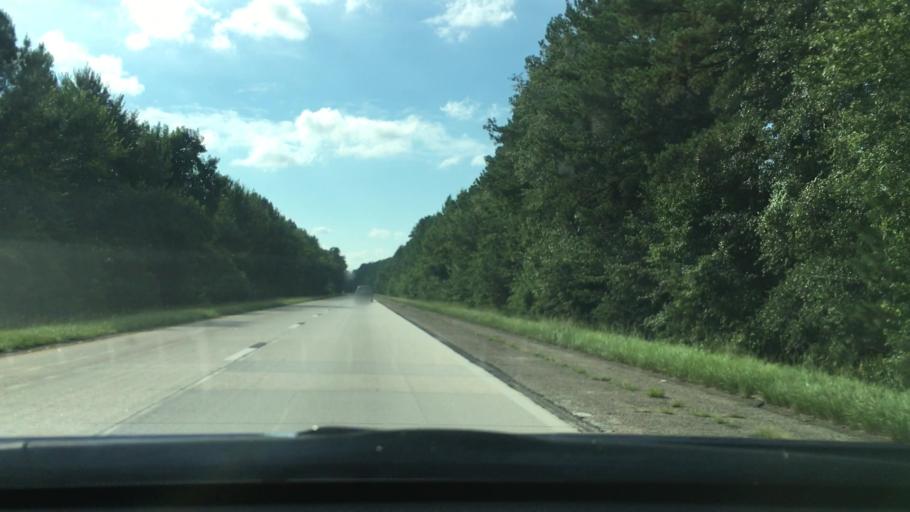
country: US
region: South Carolina
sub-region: Orangeburg County
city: Holly Hill
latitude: 33.2775
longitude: -80.4975
